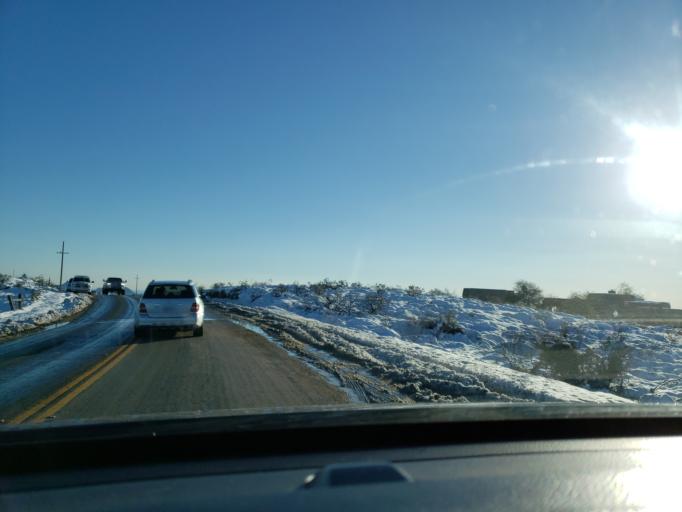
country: US
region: Arizona
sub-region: Maricopa County
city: Carefree
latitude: 33.8641
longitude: -111.8293
